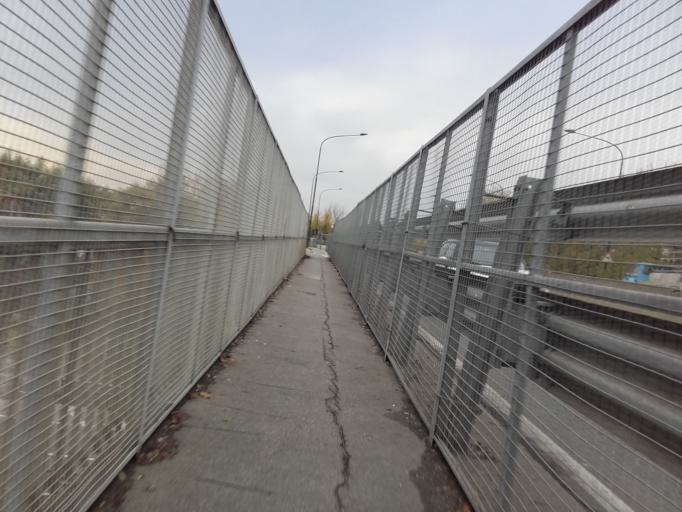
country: IT
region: Piedmont
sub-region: Provincia di Torino
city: San Mauro Torinese
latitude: 45.0948
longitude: 7.7304
